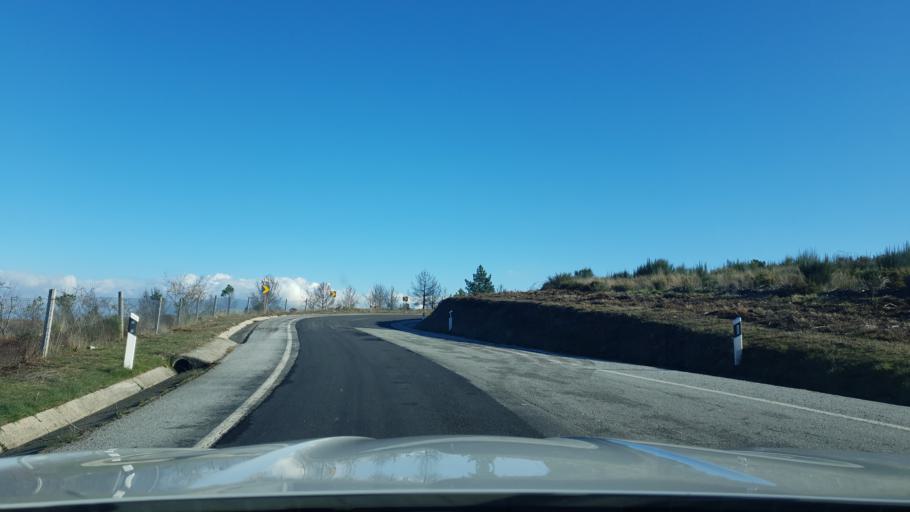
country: PT
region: Braganca
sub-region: Freixo de Espada A Cinta
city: Freixo de Espada a Cinta
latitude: 41.1583
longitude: -6.7995
